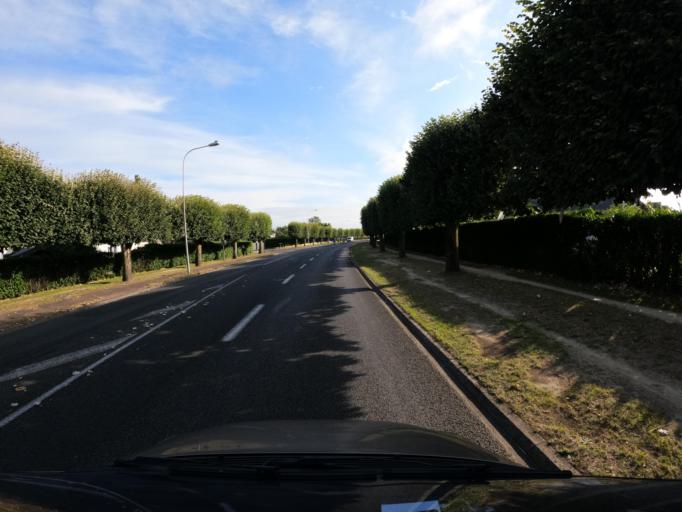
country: FR
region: Pays de la Loire
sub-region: Departement de Maine-et-Loire
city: Doue-la-Fontaine
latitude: 47.1969
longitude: -0.2862
